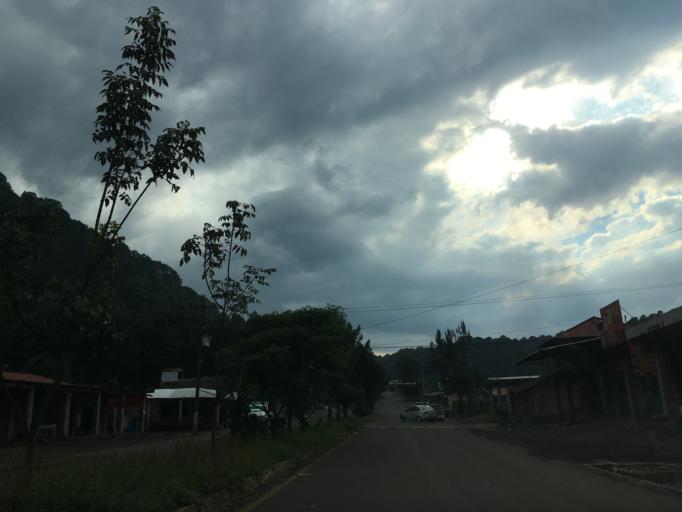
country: MX
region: Michoacan
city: Capacuaro
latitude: 19.5222
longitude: -102.1086
